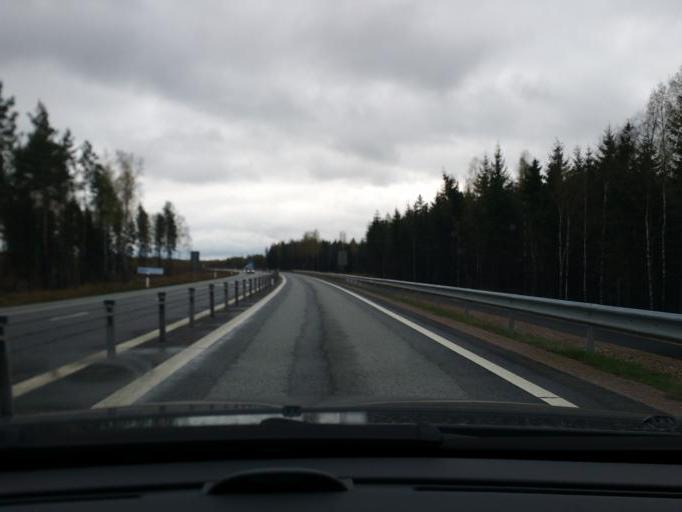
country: SE
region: Kronoberg
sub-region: Vaxjo Kommun
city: Gemla
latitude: 56.9182
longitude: 14.7171
